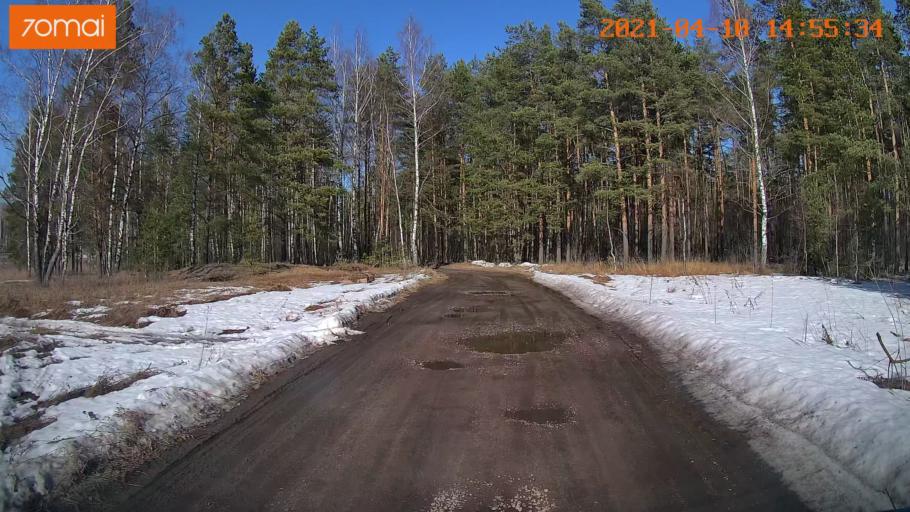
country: RU
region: Ivanovo
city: Kokhma
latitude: 56.9896
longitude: 41.0574
